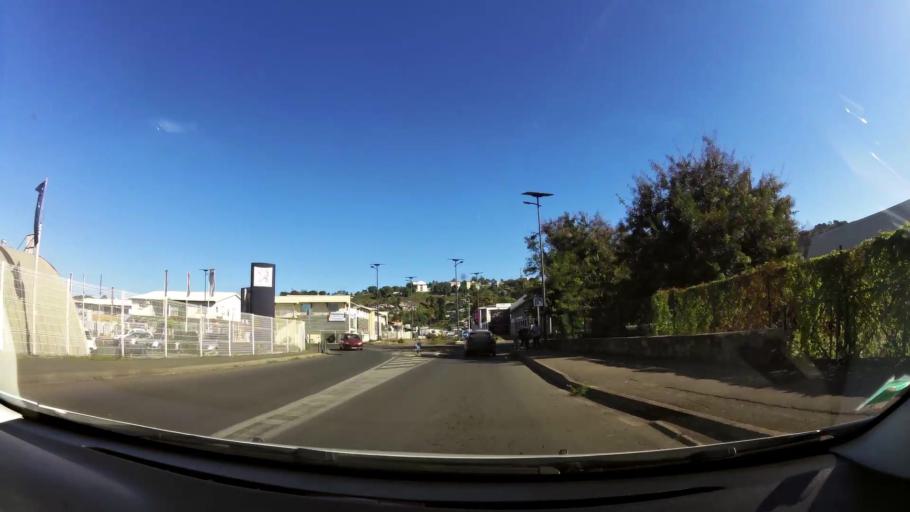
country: YT
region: Mamoudzou
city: Mamoudzou
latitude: -12.7708
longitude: 45.2236
